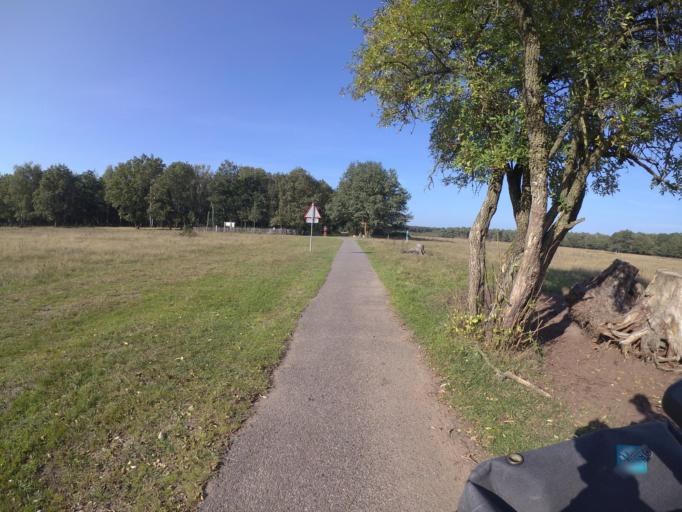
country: NL
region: North Brabant
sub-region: Gemeente Uden
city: Uden
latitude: 51.7034
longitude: 5.6240
